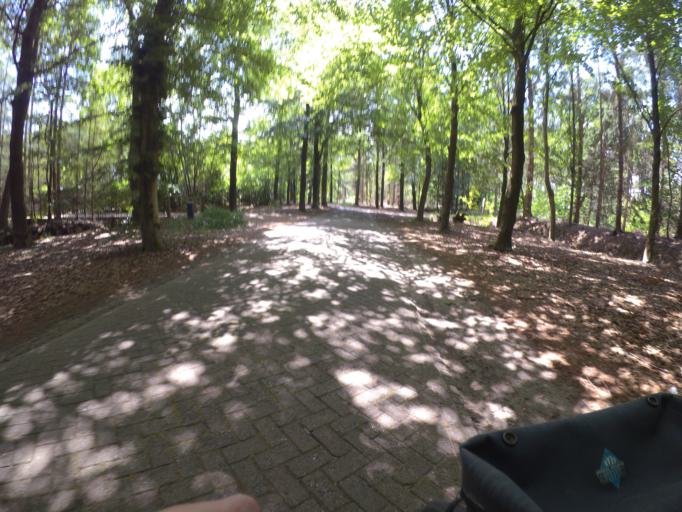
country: NL
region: North Brabant
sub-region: Gemeente Oirschot
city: Middelbeers
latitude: 51.4853
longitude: 5.2550
